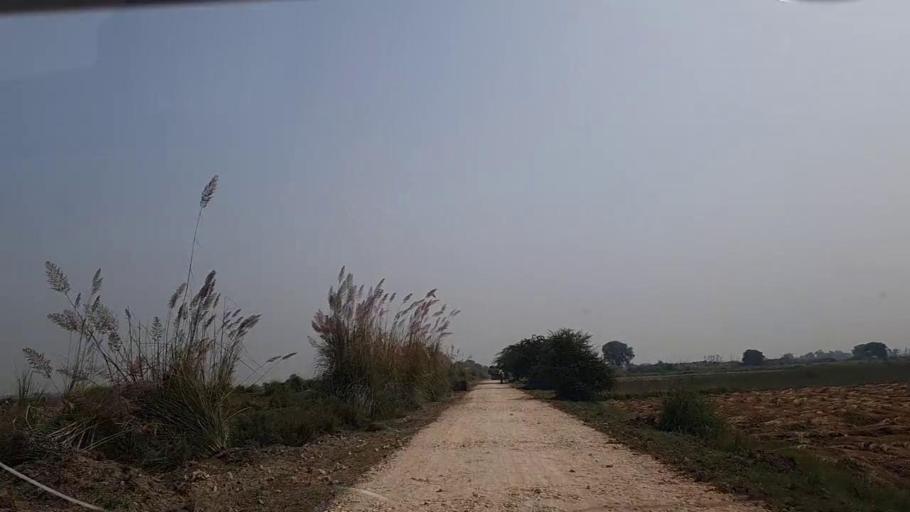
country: PK
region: Sindh
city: Garhi Yasin
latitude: 27.9209
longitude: 68.5773
